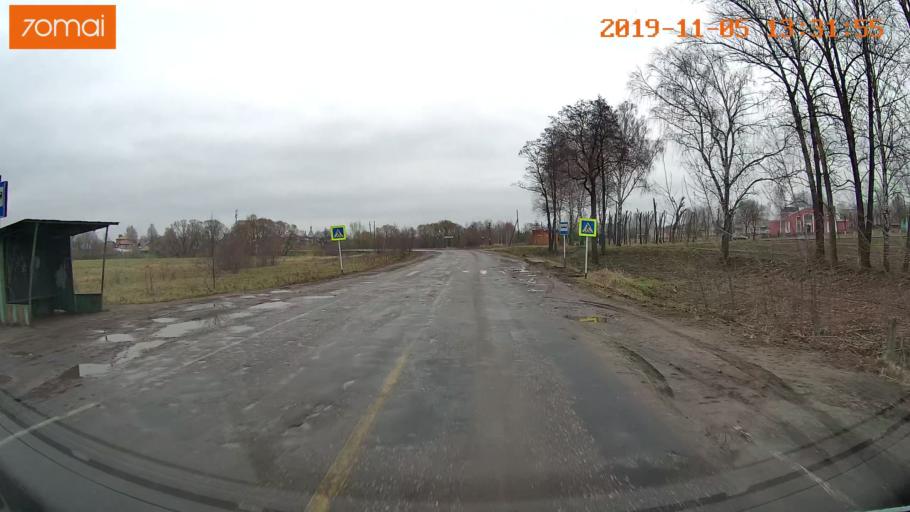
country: RU
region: Ivanovo
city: Shuya
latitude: 56.8796
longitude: 41.3968
